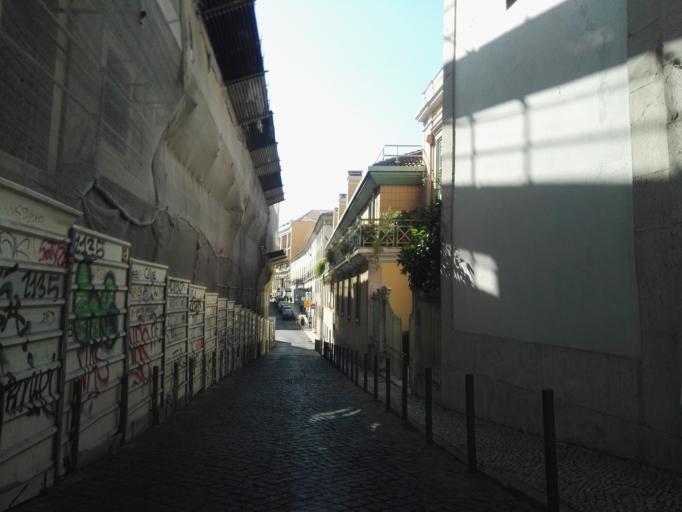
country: PT
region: Lisbon
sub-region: Lisbon
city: Lisbon
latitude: 38.7140
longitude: -9.1475
